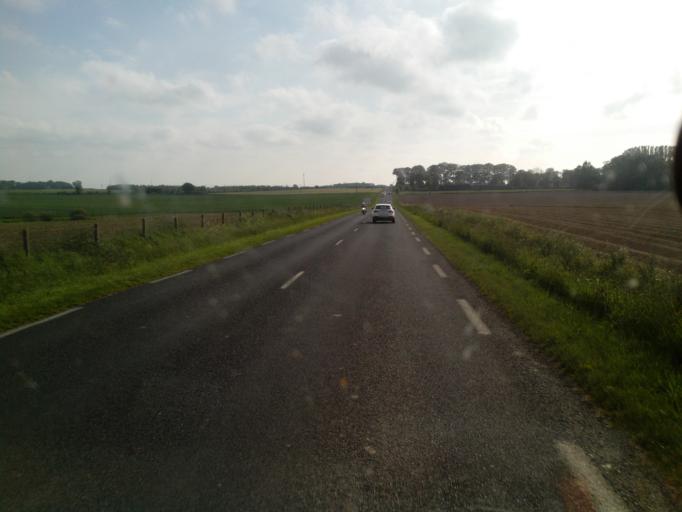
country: FR
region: Haute-Normandie
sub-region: Departement de la Seine-Maritime
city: Sainte-Marie-des-Champs
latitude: 49.6394
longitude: 0.8274
